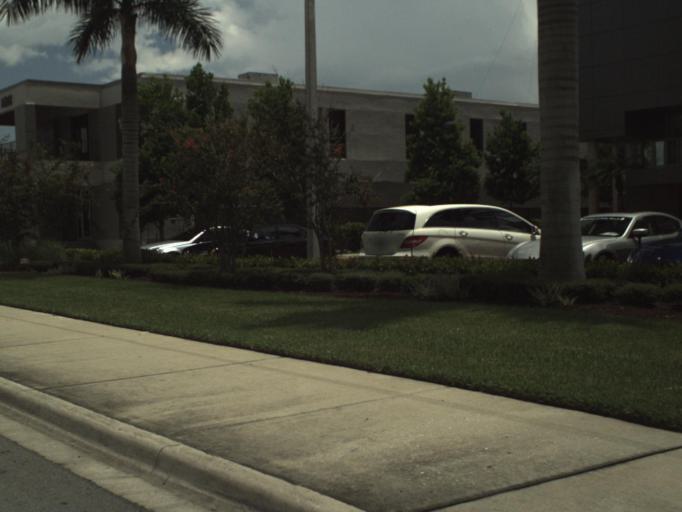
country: US
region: Florida
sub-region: Palm Beach County
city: Schall Circle
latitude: 26.7067
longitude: -80.1024
